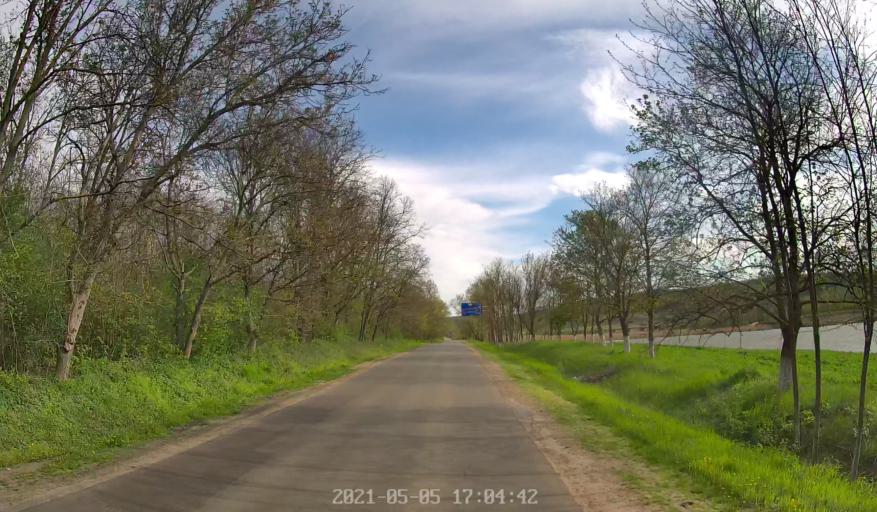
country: MD
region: Chisinau
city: Vadul lui Voda
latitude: 47.0379
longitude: 29.1363
